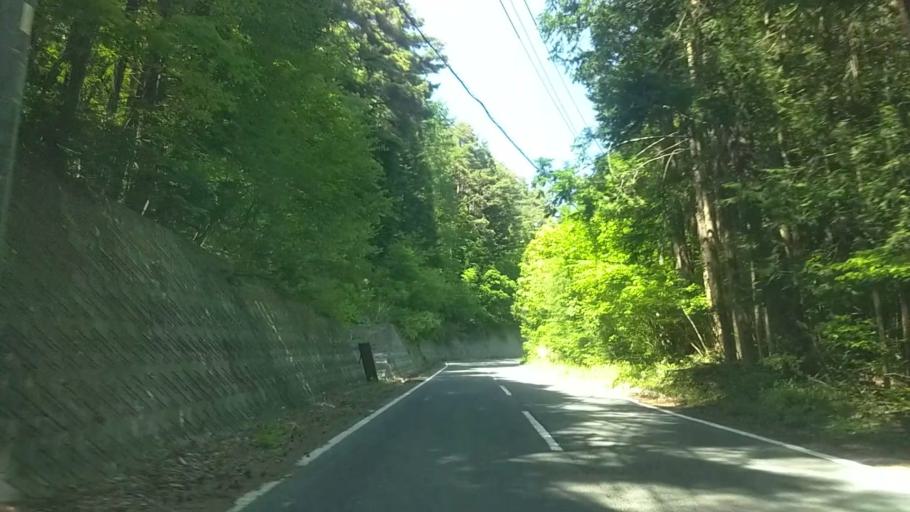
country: JP
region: Yamanashi
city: Nirasaki
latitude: 35.8633
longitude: 138.4474
